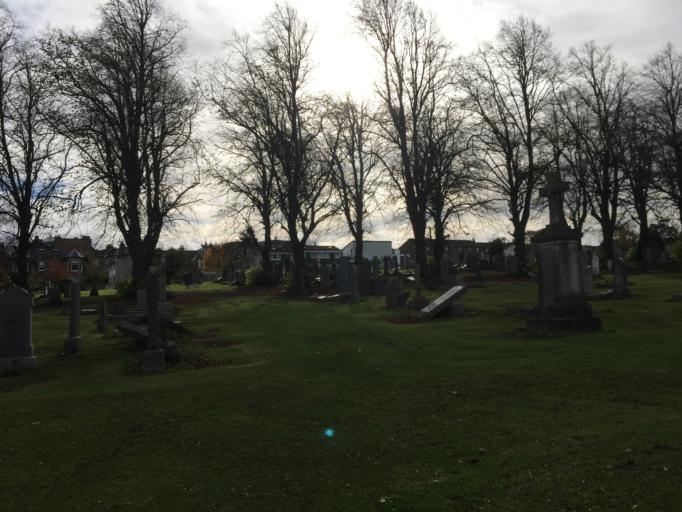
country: GB
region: Scotland
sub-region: Edinburgh
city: Edinburgh
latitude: 55.9250
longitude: -3.2131
